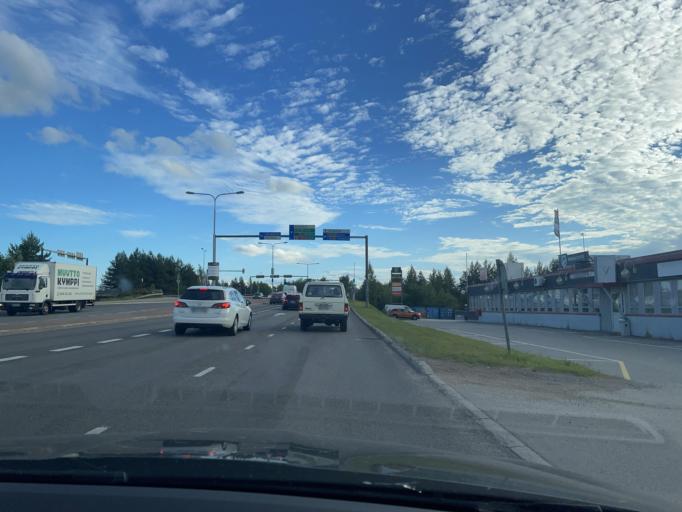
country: FI
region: Central Finland
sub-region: Jyvaeskylae
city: Jyvaeskylae
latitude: 62.2523
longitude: 25.7738
